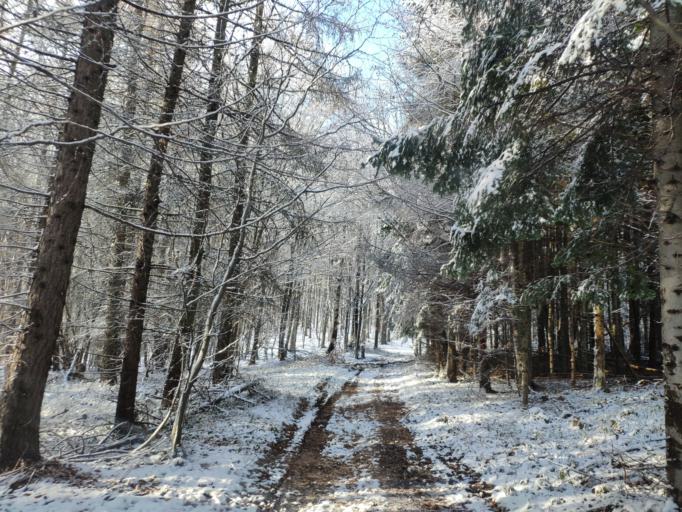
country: SK
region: Kosicky
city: Moldava nad Bodvou
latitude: 48.7428
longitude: 21.0881
